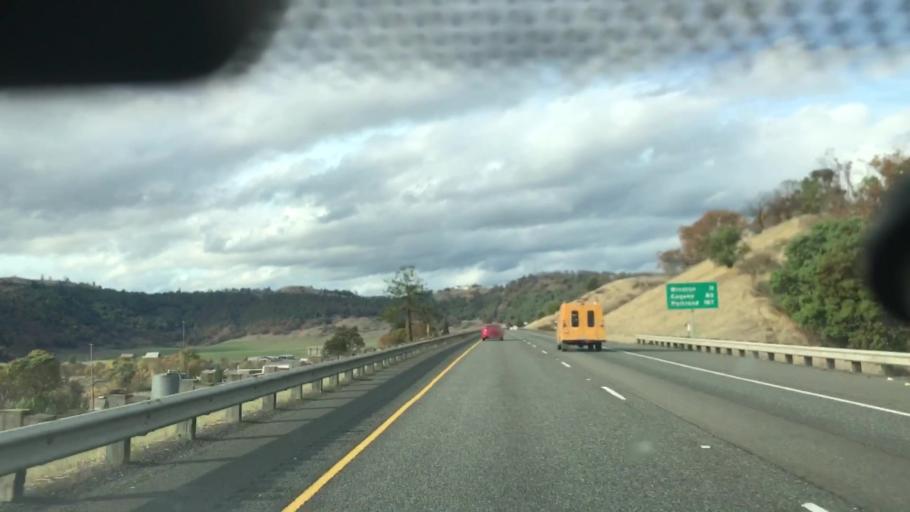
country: US
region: Oregon
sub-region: Douglas County
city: Winston
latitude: 43.0830
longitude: -123.3652
